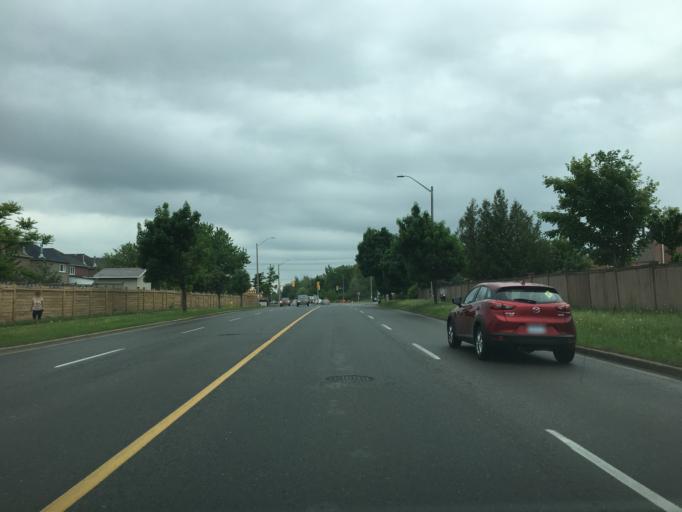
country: CA
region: Ontario
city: Markham
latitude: 43.8344
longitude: -79.2684
